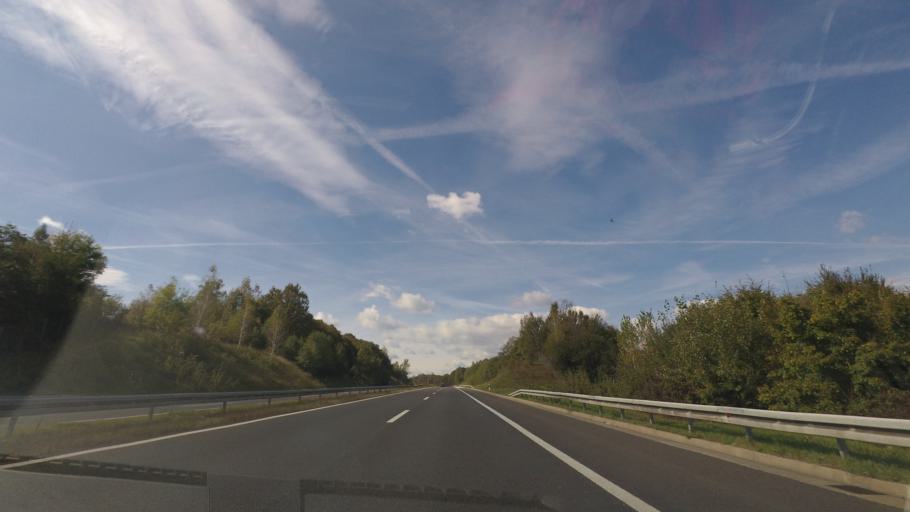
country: HR
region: Karlovacka
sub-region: Grad Karlovac
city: Karlovac
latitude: 45.5130
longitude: 15.4990
